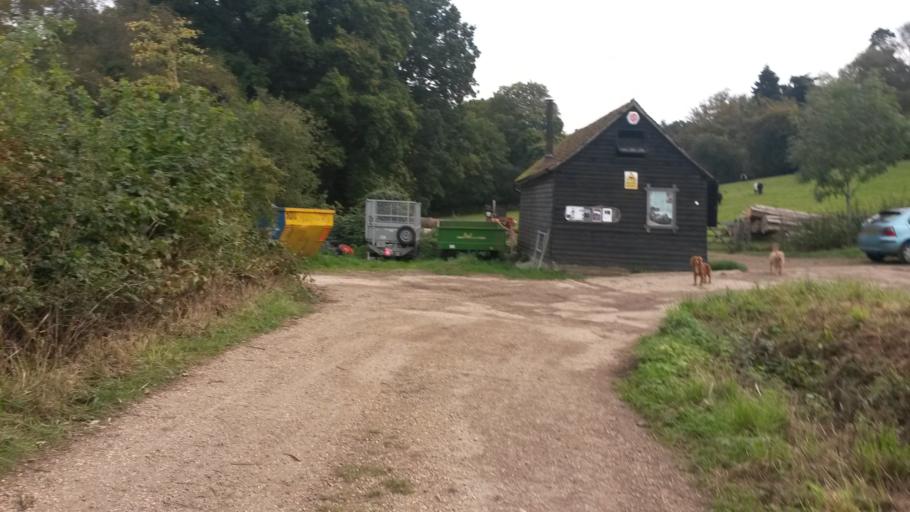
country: GB
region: England
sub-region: Surrey
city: Haslemere
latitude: 51.0871
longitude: -0.7027
